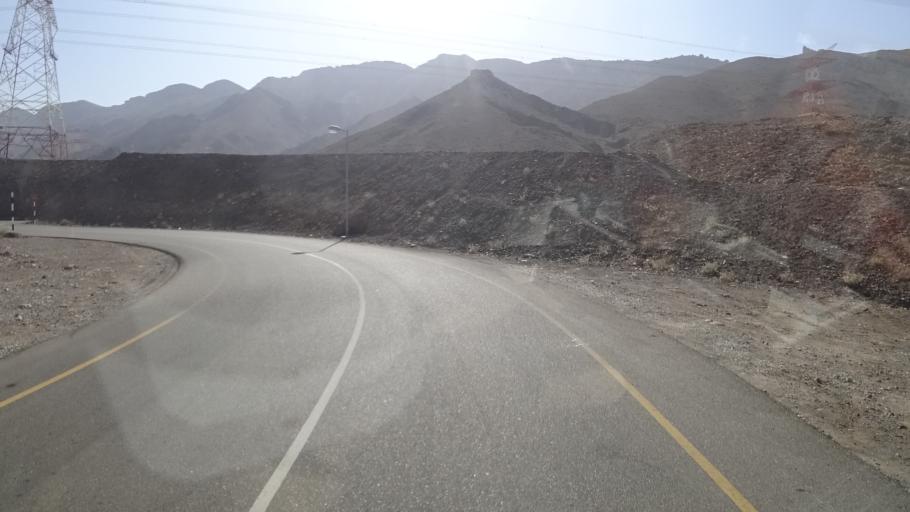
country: OM
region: Ash Sharqiyah
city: Sur
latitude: 22.6501
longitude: 59.3936
